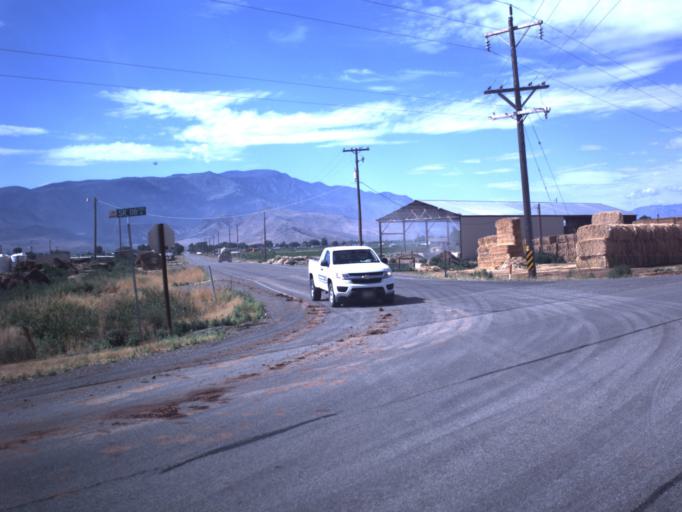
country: US
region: Utah
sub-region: Sevier County
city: Richfield
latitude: 38.8181
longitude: -112.0066
